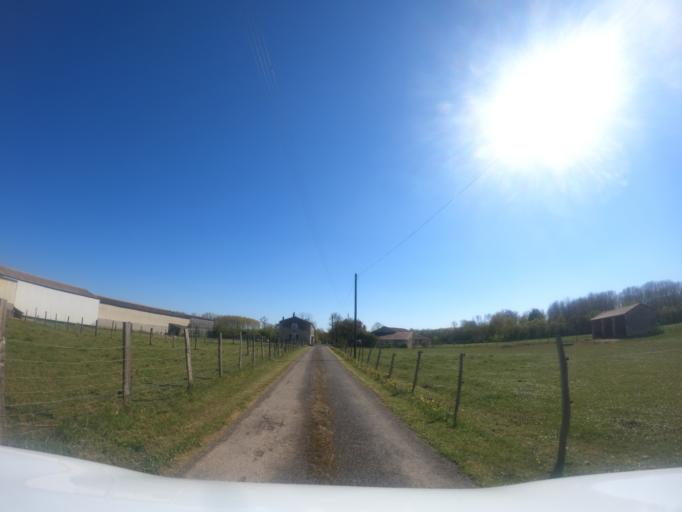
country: FR
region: Pays de la Loire
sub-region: Departement de la Vendee
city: Fontenay-le-Comte
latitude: 46.4140
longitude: -0.7955
